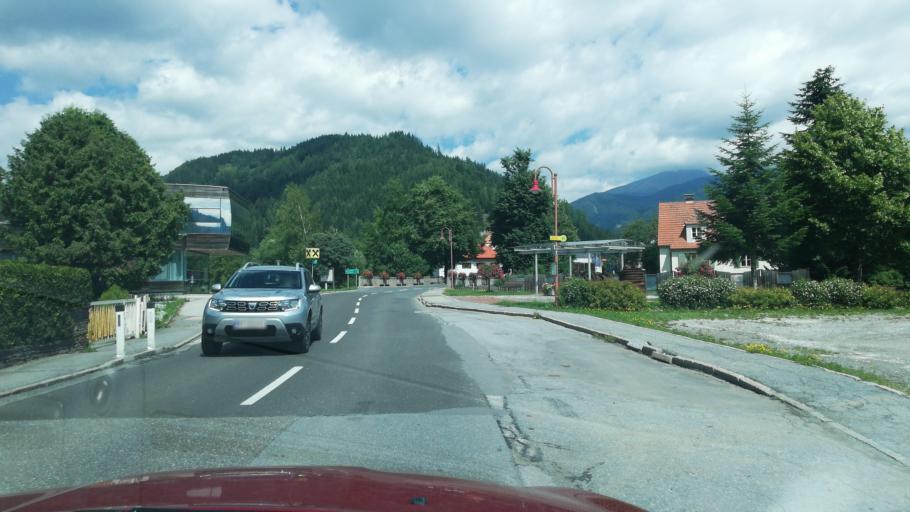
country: AT
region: Styria
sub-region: Politischer Bezirk Murtal
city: Oberzeiring
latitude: 47.2811
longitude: 14.4804
